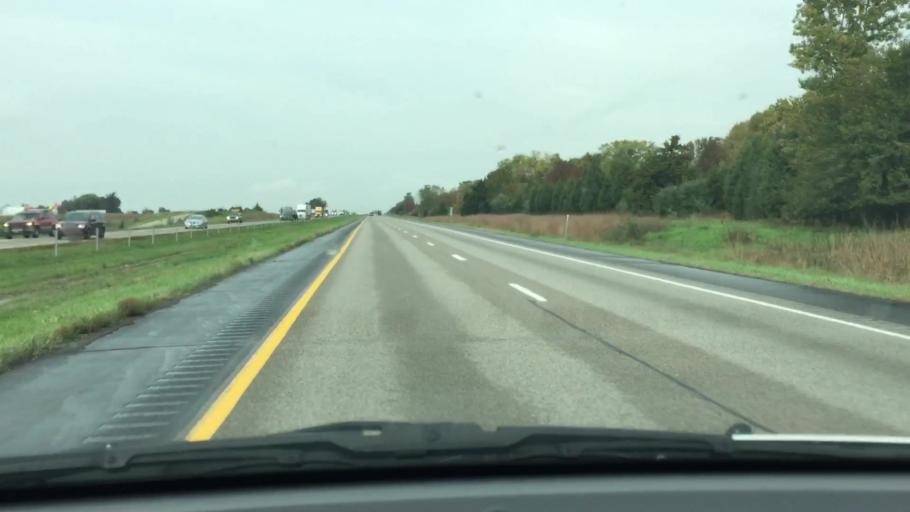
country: US
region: Iowa
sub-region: Muscatine County
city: West Liberty
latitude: 41.6475
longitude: -91.1677
